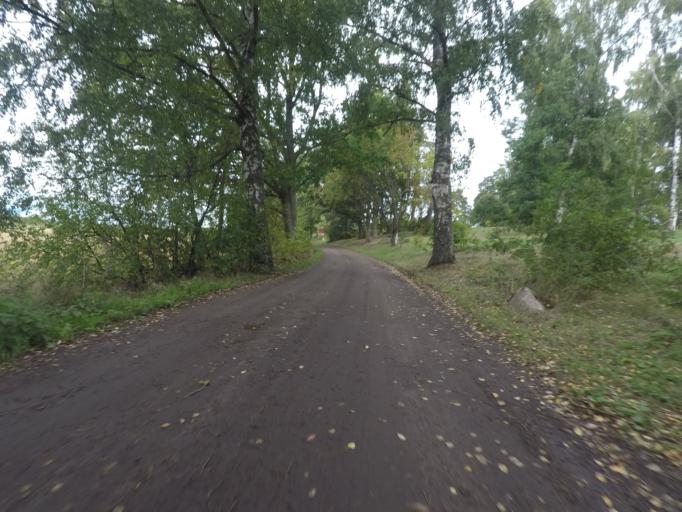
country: SE
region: Vaestmanland
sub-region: Kungsors Kommun
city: Kungsoer
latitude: 59.4590
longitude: 16.0721
